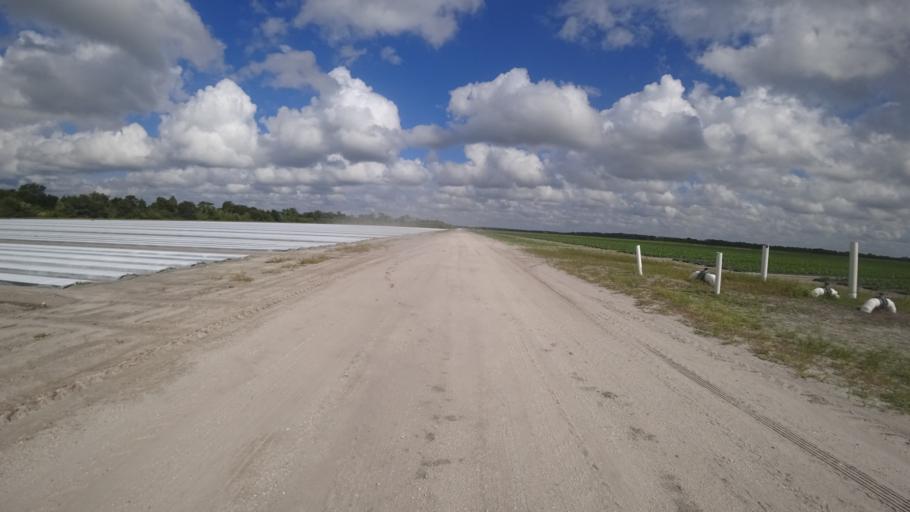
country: US
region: Florida
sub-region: Sarasota County
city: Lake Sarasota
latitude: 27.4101
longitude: -82.2113
